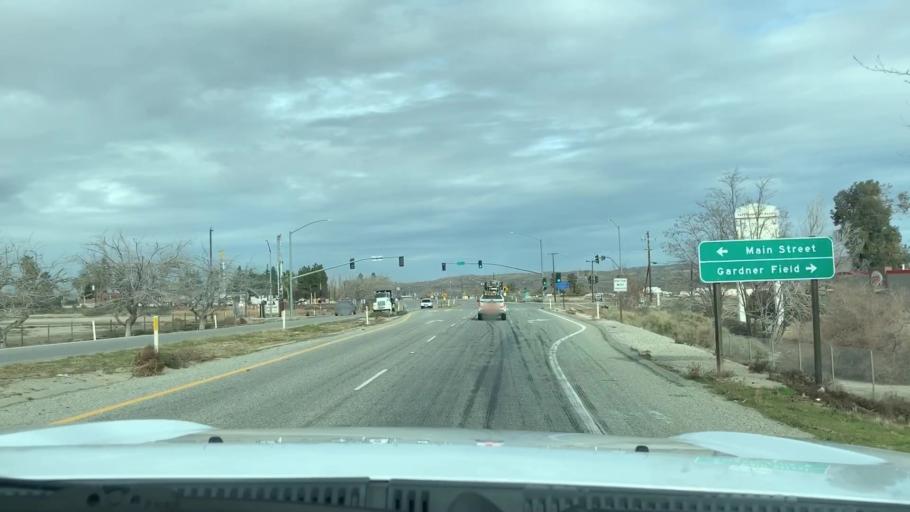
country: US
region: California
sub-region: Kern County
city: South Taft
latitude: 35.1359
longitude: -119.4474
